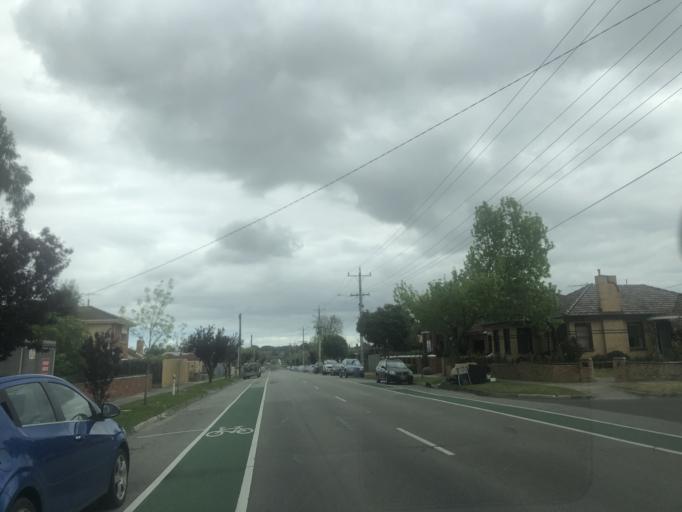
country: AU
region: Victoria
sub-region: Greater Dandenong
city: Dandenong
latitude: -37.9809
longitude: 145.2158
